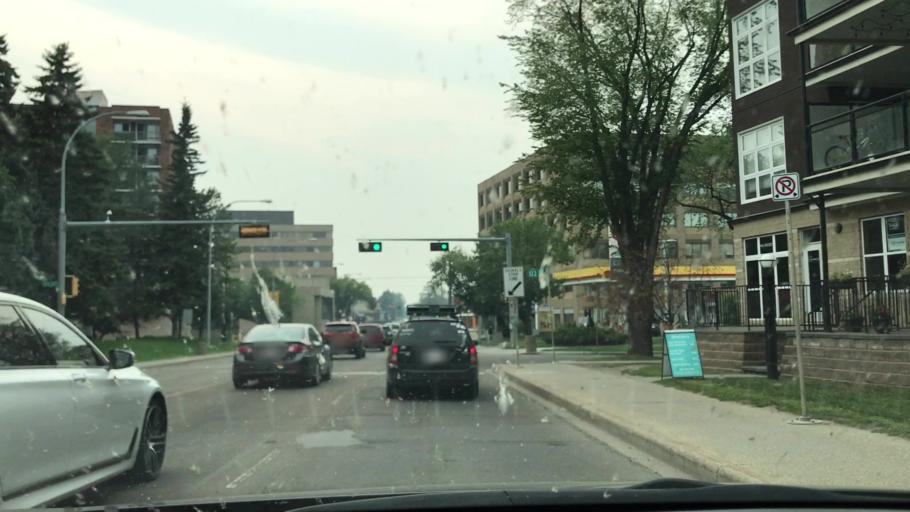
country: CA
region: Alberta
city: Edmonton
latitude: 53.5464
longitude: -113.5318
